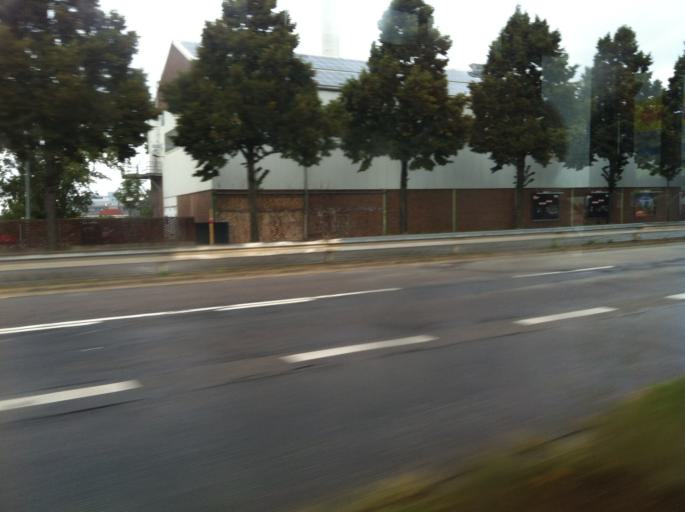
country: DE
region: Rheinland-Pfalz
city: Mainz
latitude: 50.0232
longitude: 8.2362
